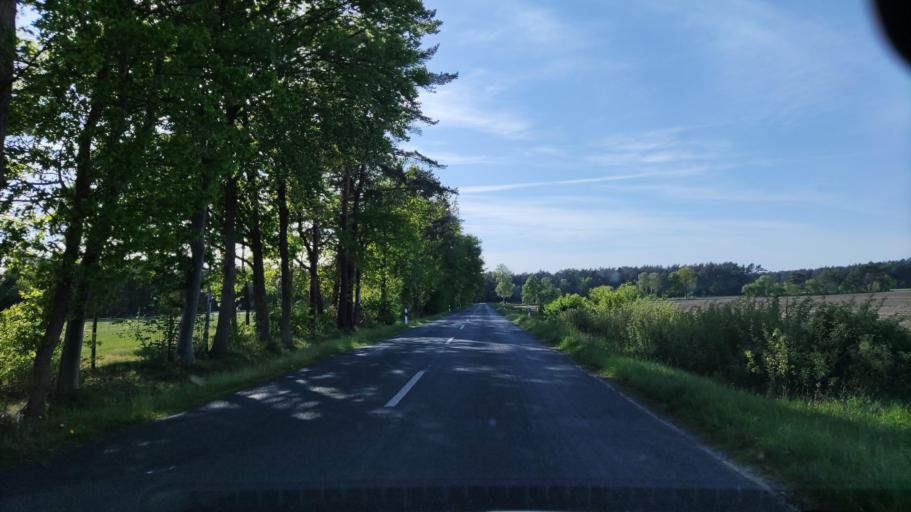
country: DE
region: Lower Saxony
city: Welle
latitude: 53.1798
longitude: 9.7767
